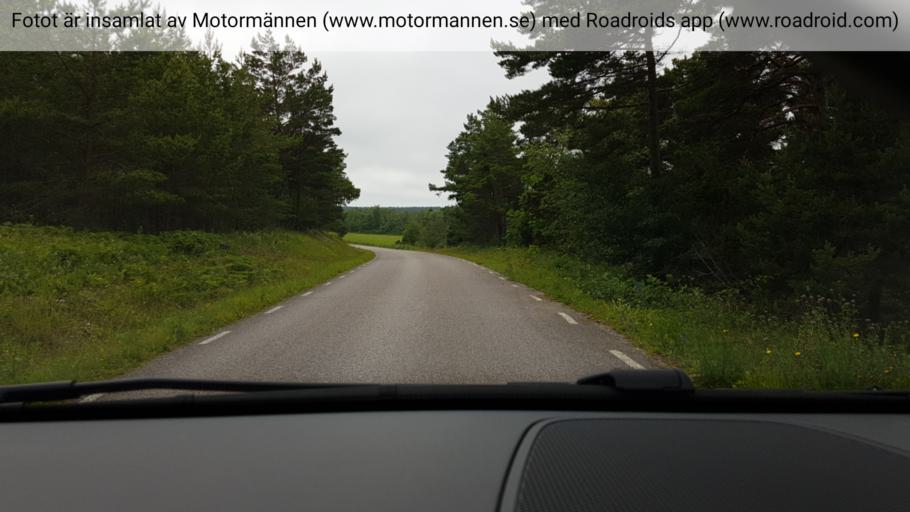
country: SE
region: Gotland
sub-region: Gotland
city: Slite
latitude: 57.9197
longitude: 18.7286
